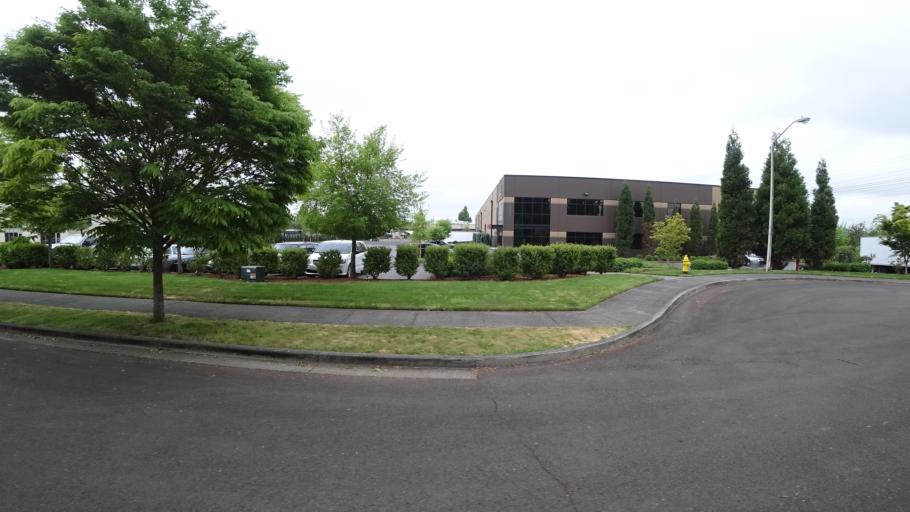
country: US
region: Oregon
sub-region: Washington County
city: Rockcreek
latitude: 45.5670
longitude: -122.8982
